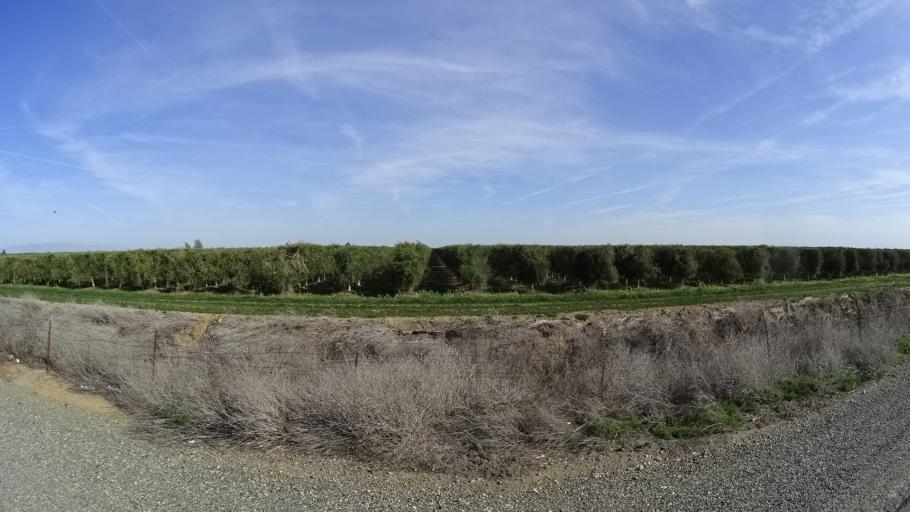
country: US
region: California
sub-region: Glenn County
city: Willows
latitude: 39.6244
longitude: -122.2128
